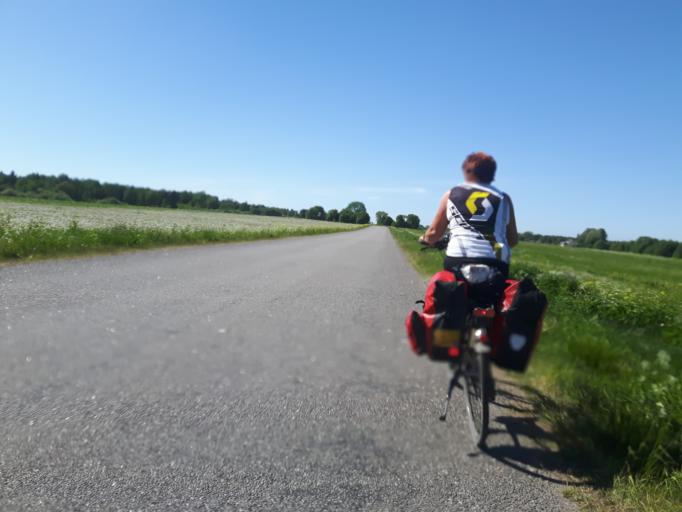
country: EE
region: Laeaene-Virumaa
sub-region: Haljala vald
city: Haljala
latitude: 59.5401
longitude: 26.2286
